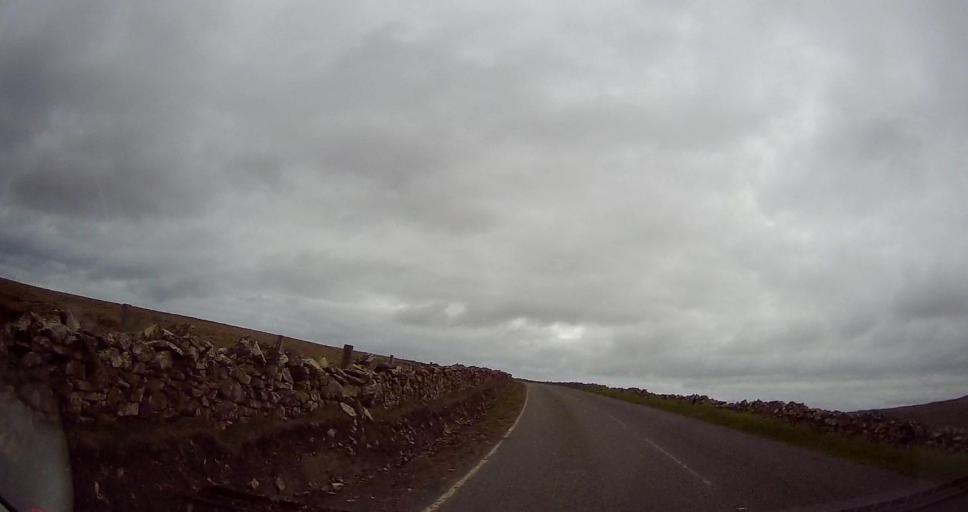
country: GB
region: Scotland
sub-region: Shetland Islands
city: Shetland
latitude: 60.7529
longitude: -0.8850
